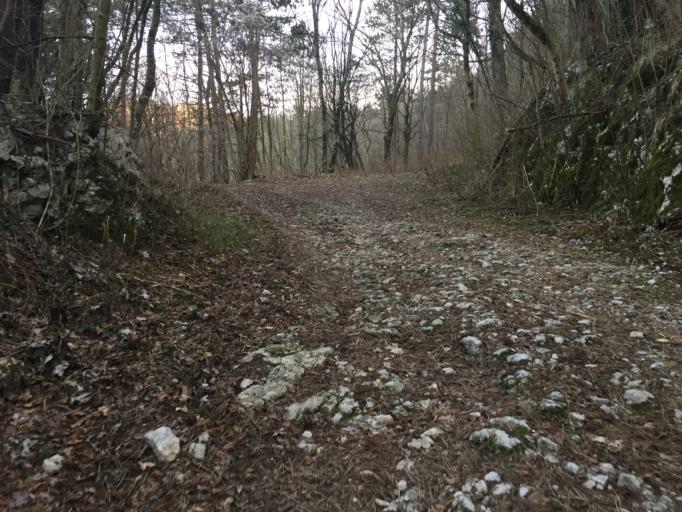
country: SI
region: Kanal
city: Kanal
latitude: 46.0432
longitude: 13.6750
